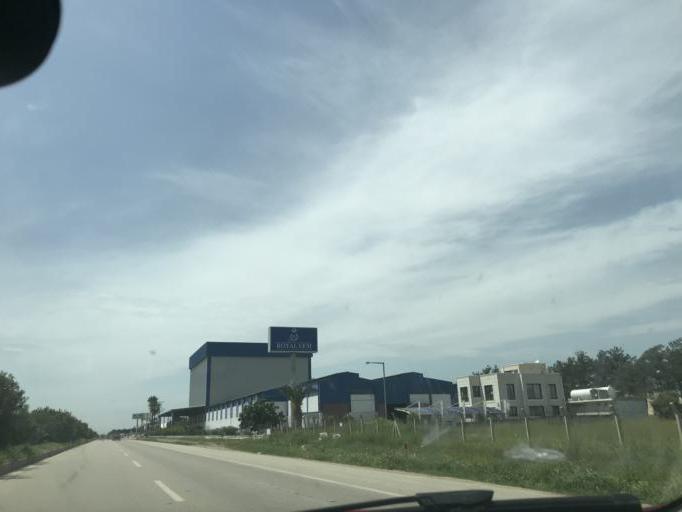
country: TR
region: Adana
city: Yakapinar
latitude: 36.9700
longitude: 35.5327
